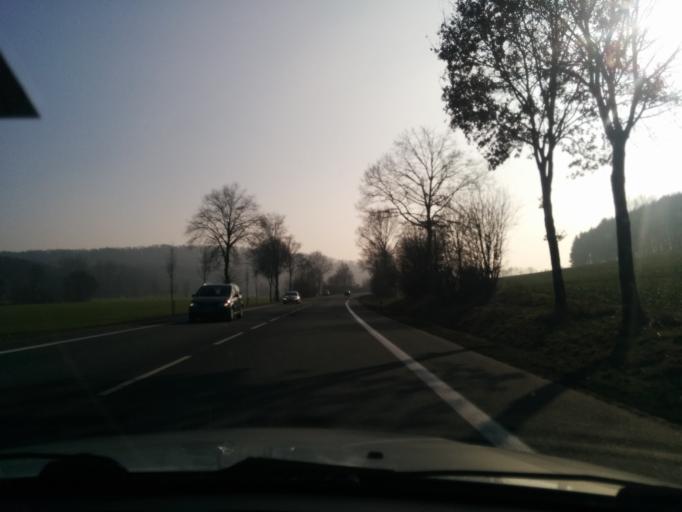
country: DE
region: North Rhine-Westphalia
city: Brakel
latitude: 51.7530
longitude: 9.1768
